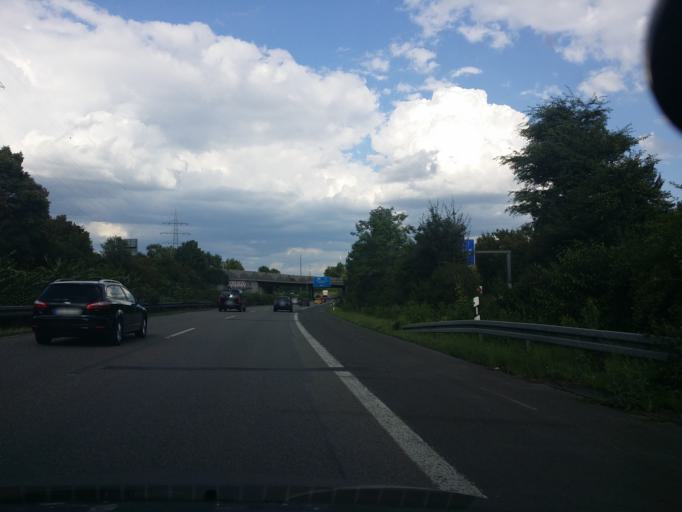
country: DE
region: Hesse
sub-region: Regierungsbezirk Darmstadt
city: Eschborn
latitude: 50.1288
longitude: 8.5687
